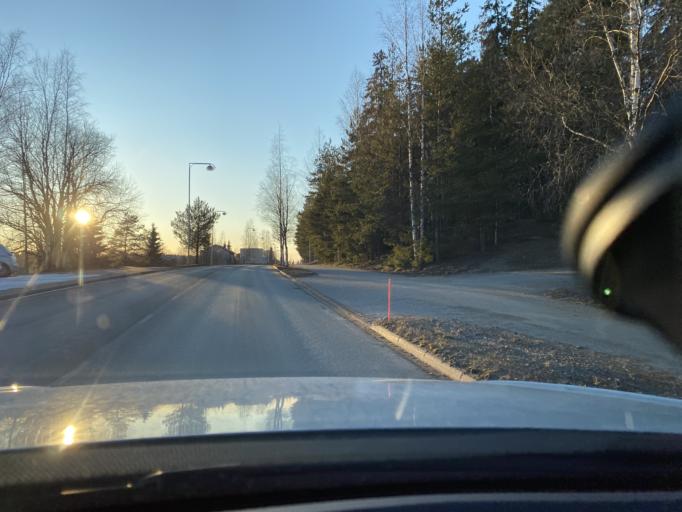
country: FI
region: Pirkanmaa
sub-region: Lounais-Pirkanmaa
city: Punkalaidun
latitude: 61.1100
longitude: 23.1162
